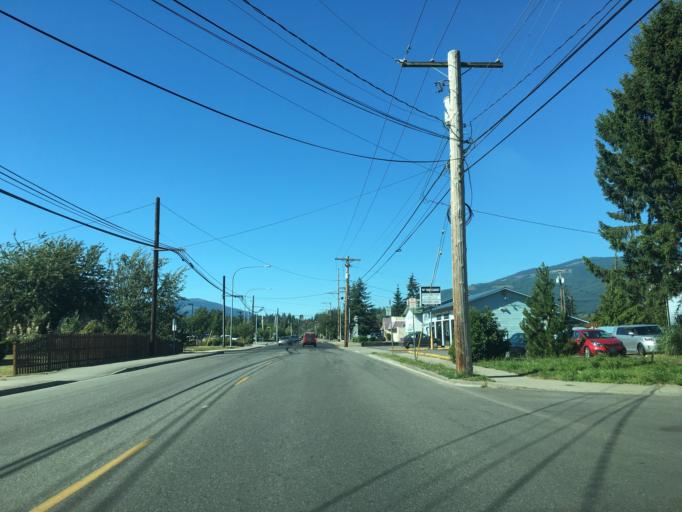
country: US
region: Washington
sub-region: Skagit County
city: Sedro-Woolley
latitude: 48.5089
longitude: -122.2258
